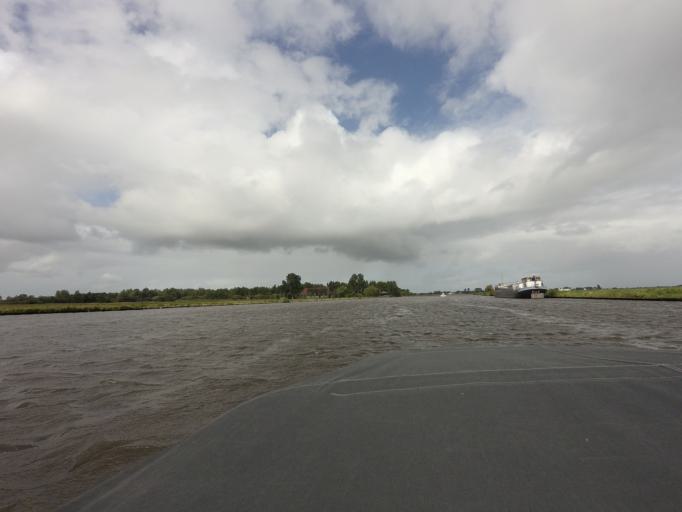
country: NL
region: Friesland
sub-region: Gemeente Boarnsterhim
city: Warten
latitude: 53.1371
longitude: 5.9164
